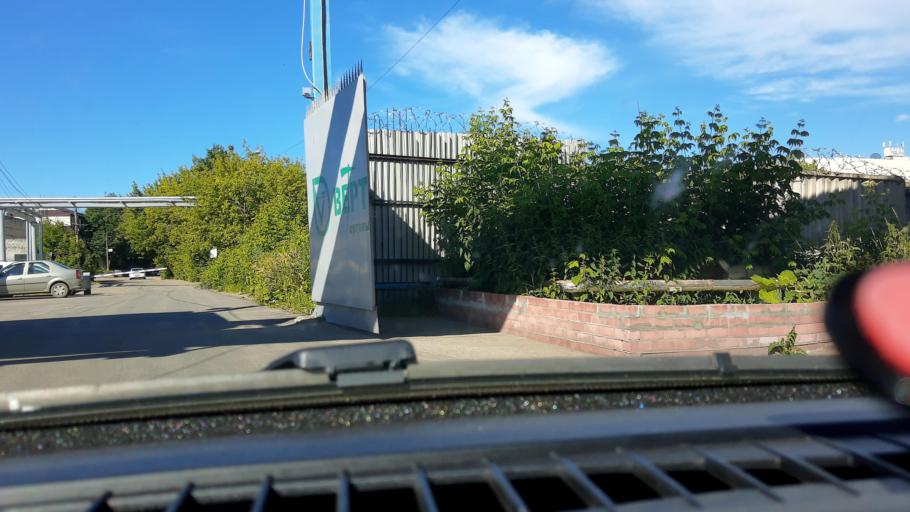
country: RU
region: Nizjnij Novgorod
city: Gorbatovka
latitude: 56.2423
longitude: 43.8736
